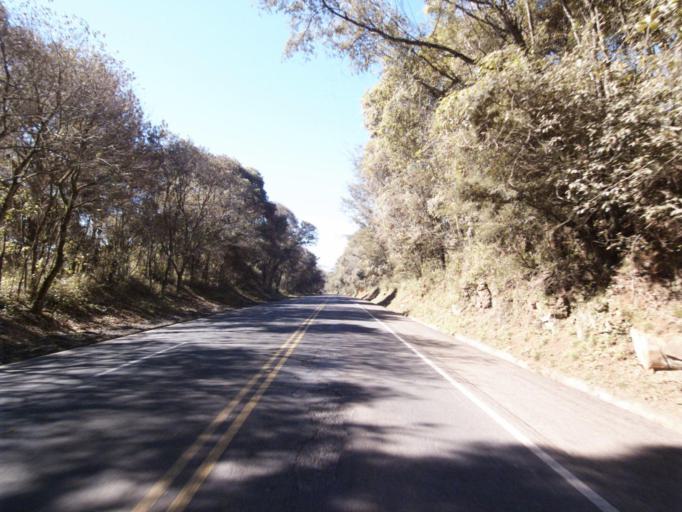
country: BR
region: Santa Catarina
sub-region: Sao Lourenco Do Oeste
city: Sao Lourenco dOeste
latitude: -26.8261
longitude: -53.0608
